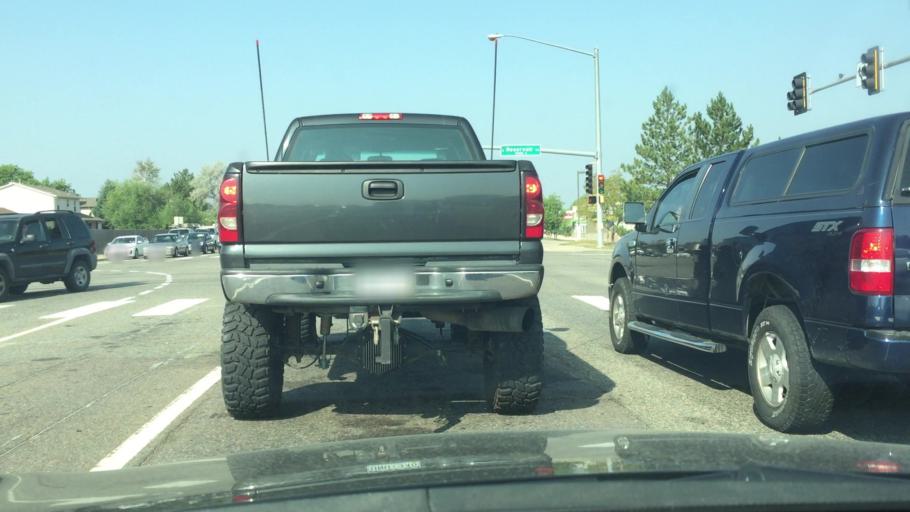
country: US
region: Colorado
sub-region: Arapahoe County
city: Dove Valley
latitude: 39.6385
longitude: -104.7629
